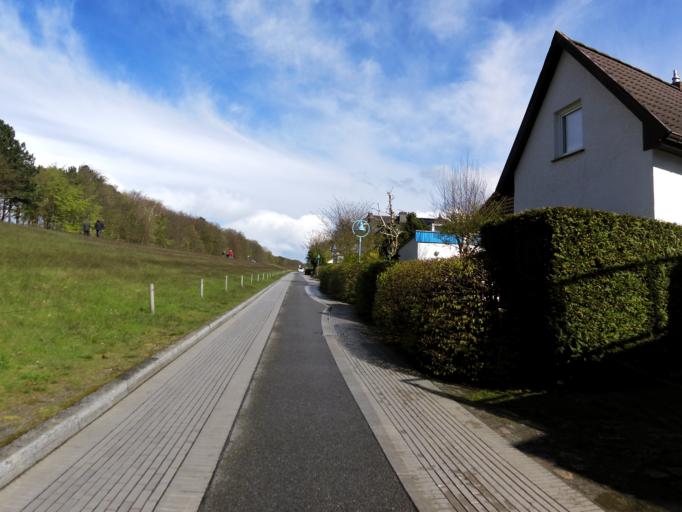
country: DE
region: Mecklenburg-Vorpommern
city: Zingst
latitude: 54.4409
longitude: 12.6897
